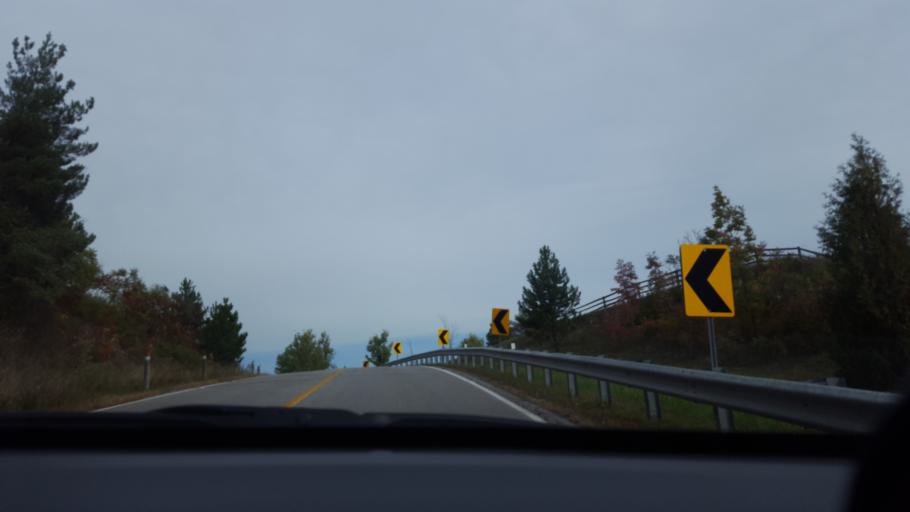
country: CA
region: Ontario
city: Newmarket
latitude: 44.0291
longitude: -79.5541
